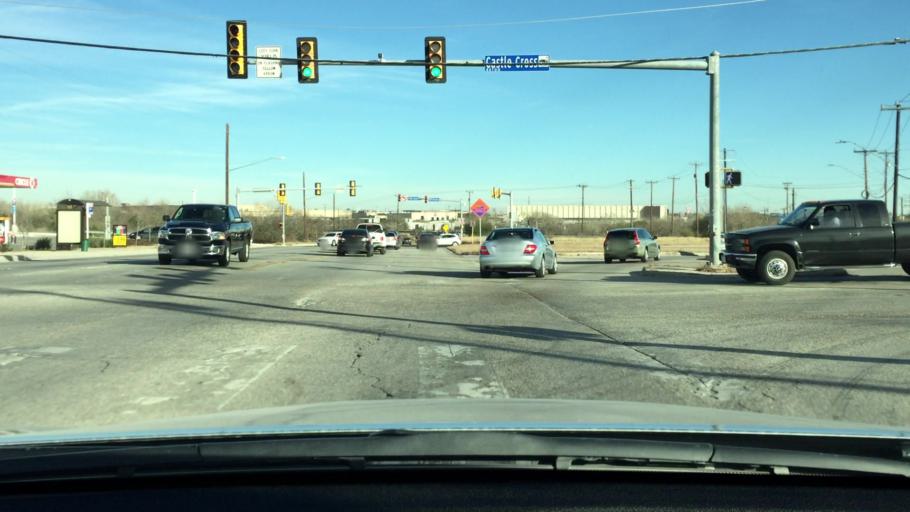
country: US
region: Texas
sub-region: Bexar County
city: Kirby
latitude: 29.4840
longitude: -98.3719
